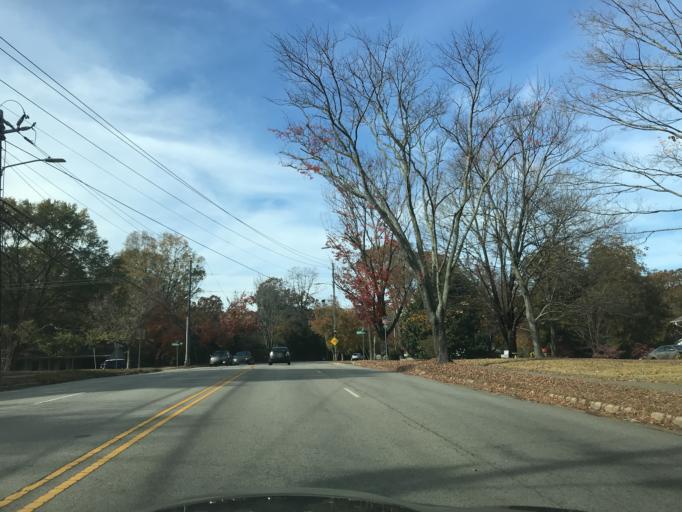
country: US
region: North Carolina
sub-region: Wake County
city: West Raleigh
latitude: 35.8519
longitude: -78.6334
